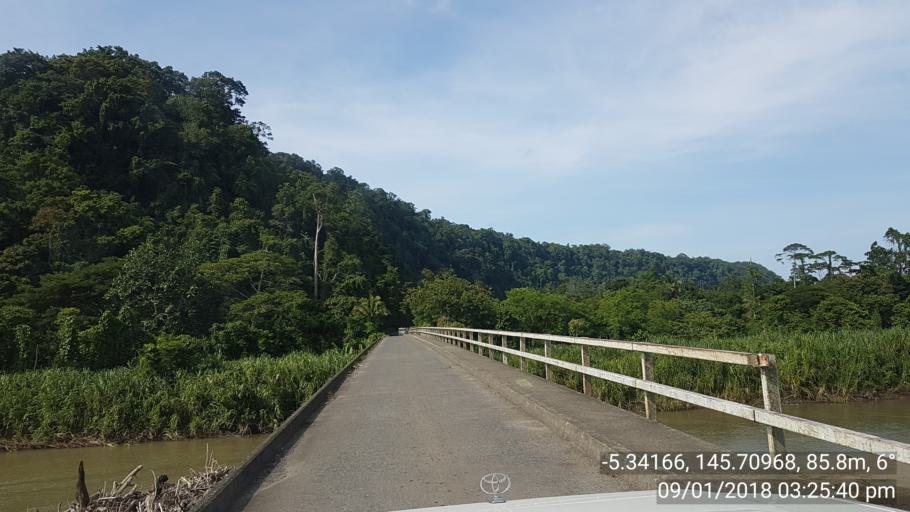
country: PG
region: Madang
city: Madang
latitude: -5.3418
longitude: 145.7097
